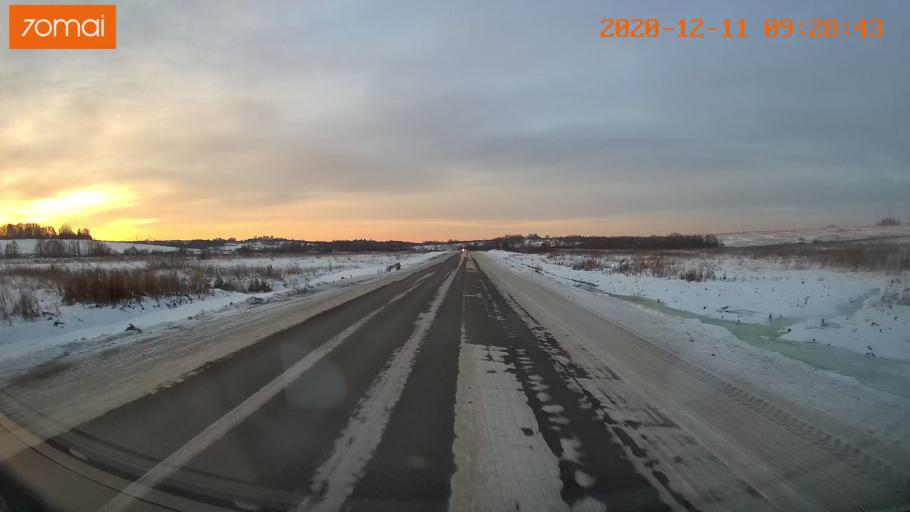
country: RU
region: Vologda
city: Vologda
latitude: 59.1501
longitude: 40.0065
